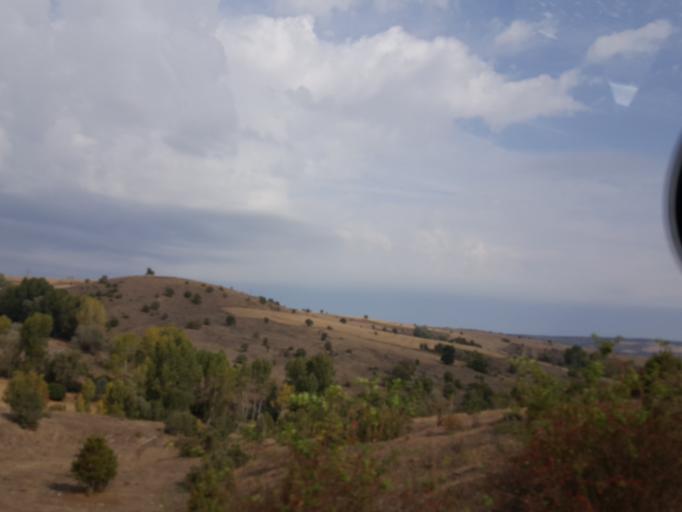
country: TR
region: Tokat
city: Zile
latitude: 40.3979
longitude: 35.8574
